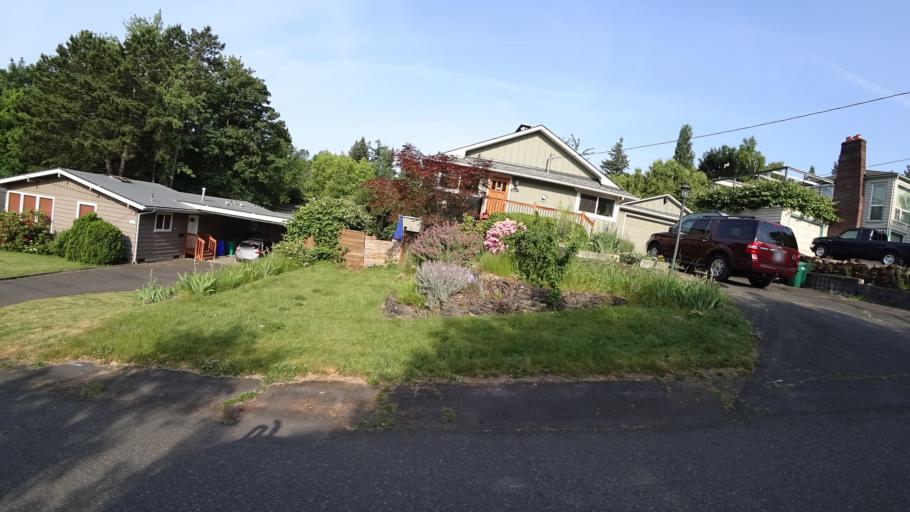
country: US
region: Oregon
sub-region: Washington County
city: Garden Home-Whitford
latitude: 45.4611
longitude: -122.7135
